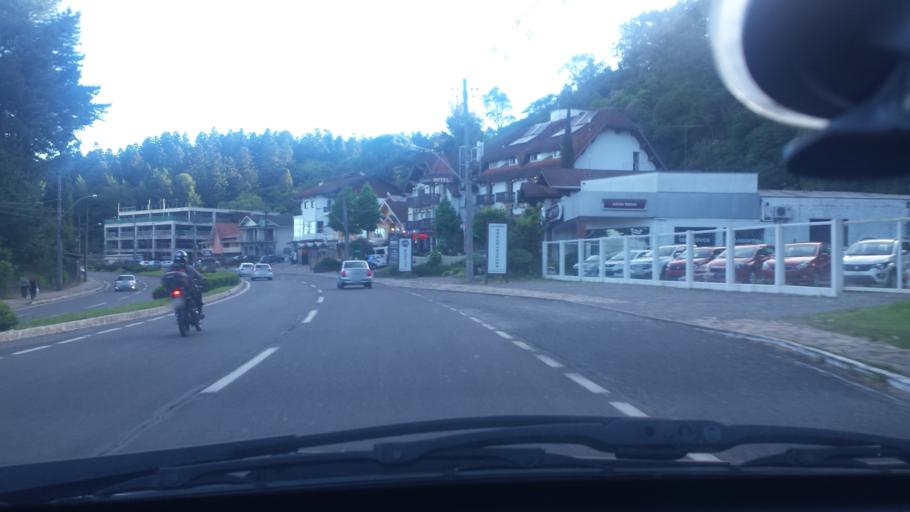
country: BR
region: Rio Grande do Sul
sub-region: Canela
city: Canela
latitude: -29.3731
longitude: -50.8646
